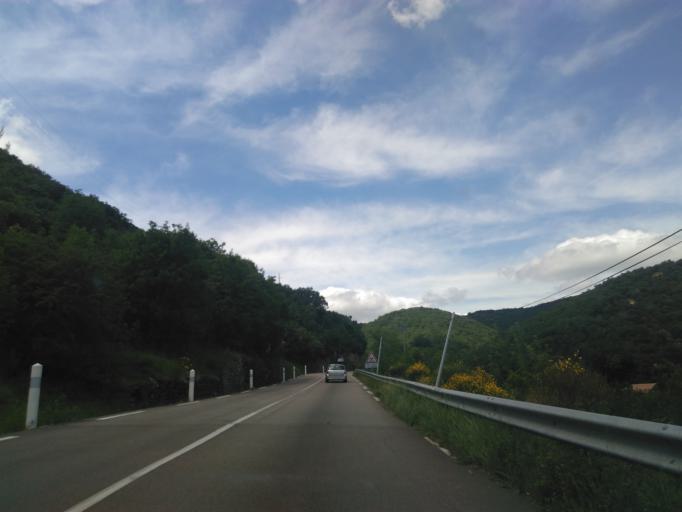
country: FR
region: Rhone-Alpes
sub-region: Departement de l'Ardeche
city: Le Teil
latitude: 44.5542
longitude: 4.6559
